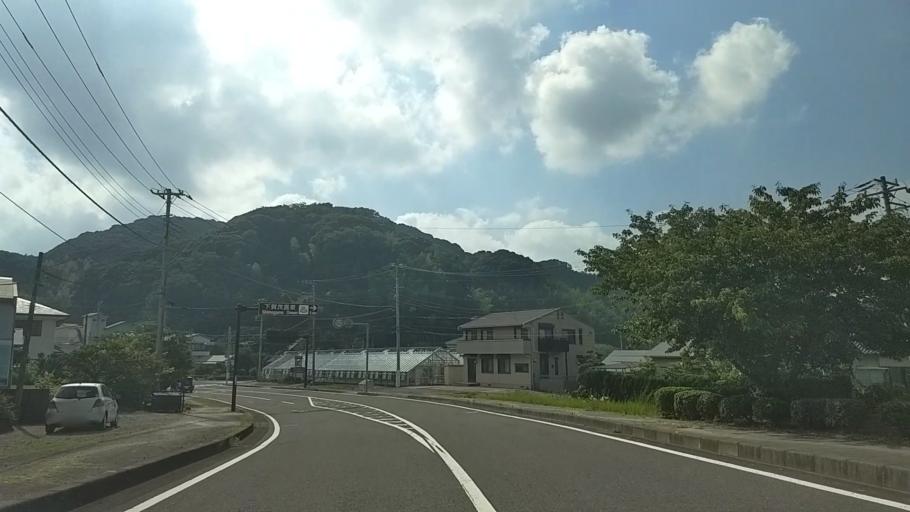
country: JP
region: Shizuoka
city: Shimoda
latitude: 34.6493
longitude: 138.8581
